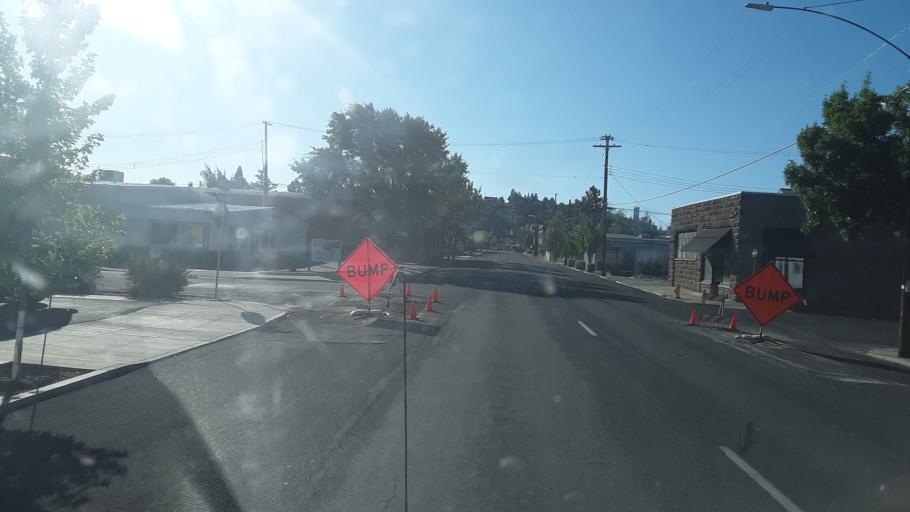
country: US
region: Oregon
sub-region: Klamath County
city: Klamath Falls
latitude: 42.2225
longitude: -121.7789
